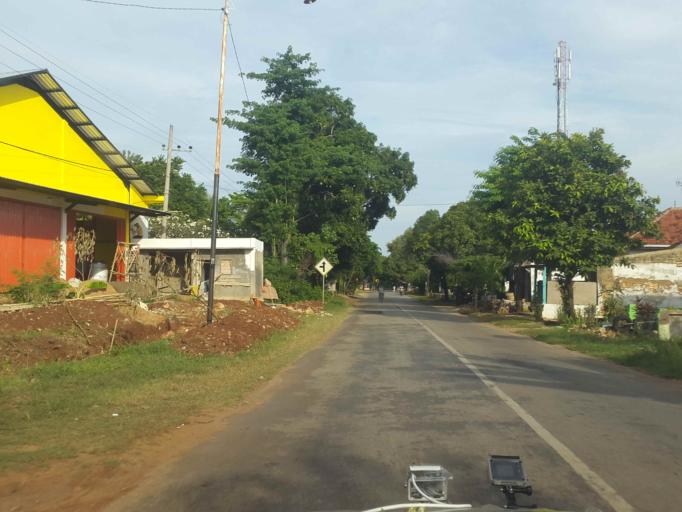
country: ID
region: East Java
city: Kebunkelapa
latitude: -7.0446
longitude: 113.9248
